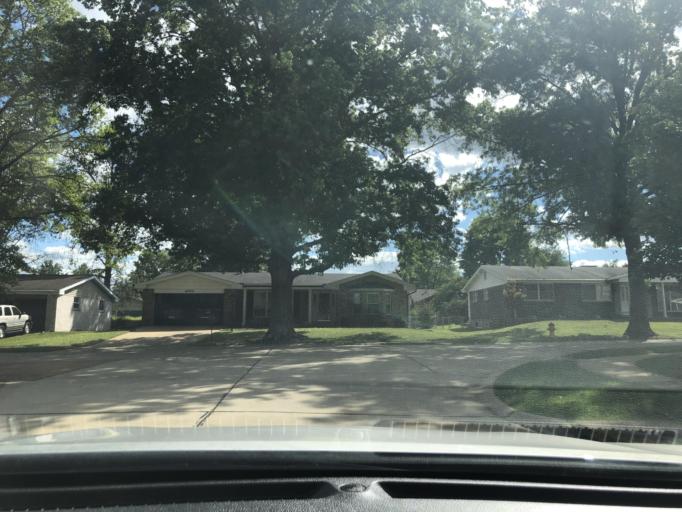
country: US
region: Missouri
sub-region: Saint Louis County
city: Concord
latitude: 38.5012
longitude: -90.3536
